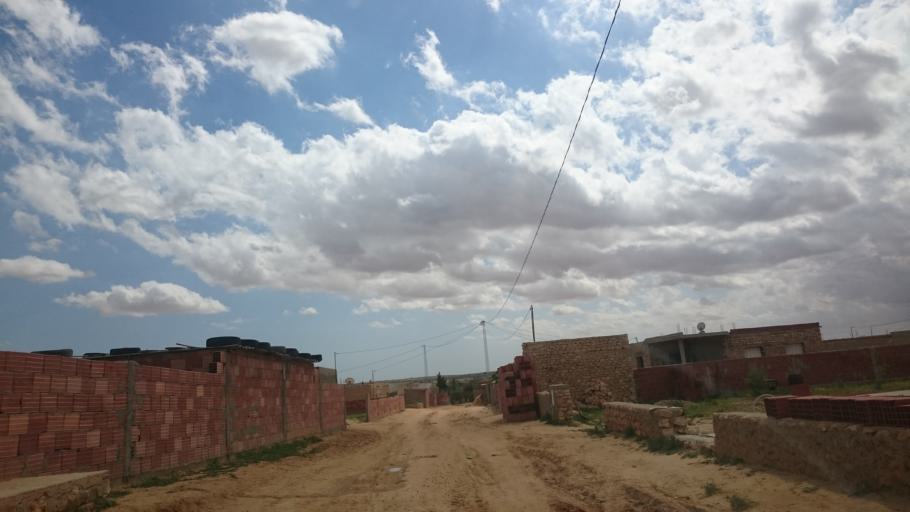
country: TN
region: Safaqis
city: Sfax
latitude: 34.7466
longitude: 10.4852
